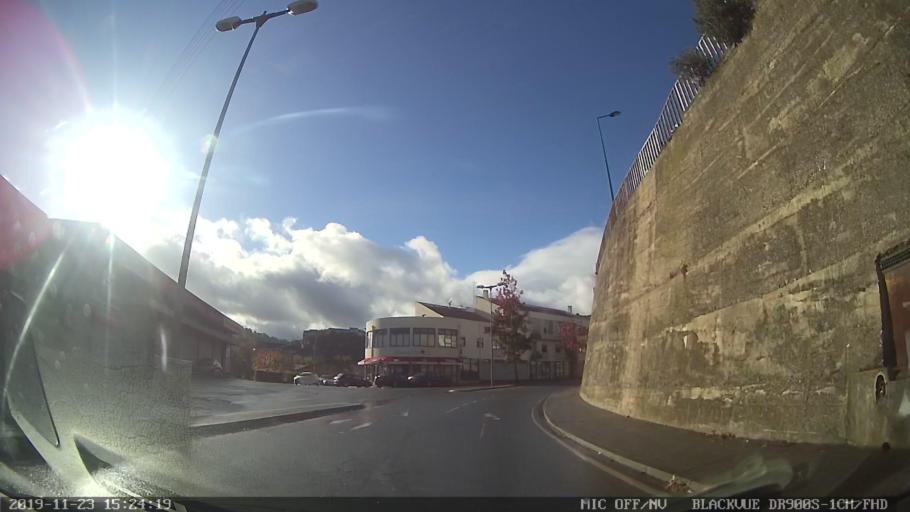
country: PT
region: Viseu
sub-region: Lamego
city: Lamego
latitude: 41.0991
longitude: -7.8038
